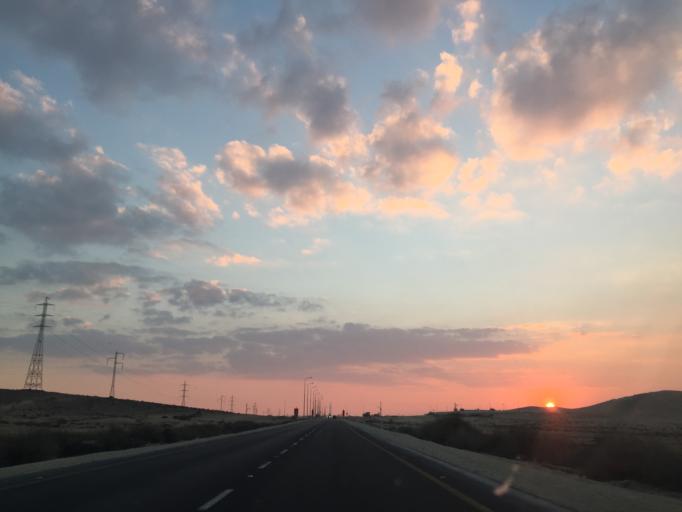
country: IL
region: Southern District
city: Yeroham
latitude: 31.0278
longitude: 34.7981
